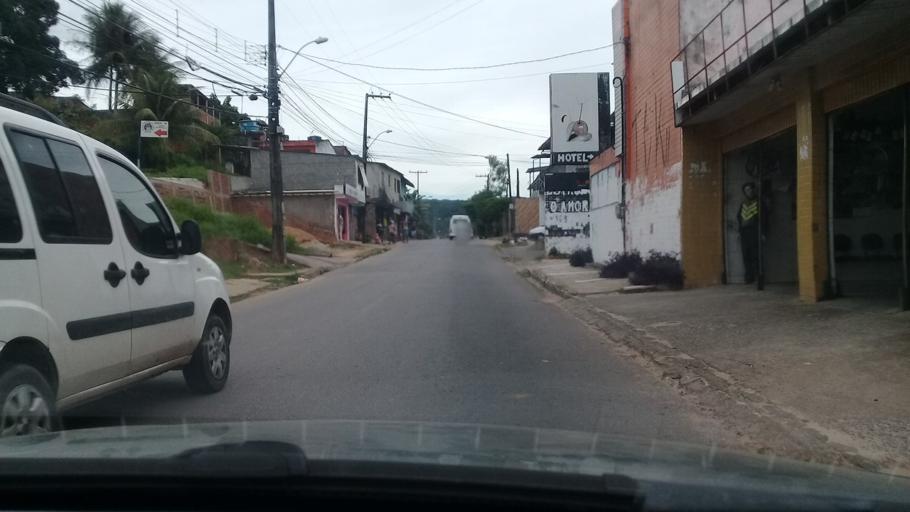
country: BR
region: Pernambuco
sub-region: Sao Lourenco Da Mata
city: Sao Lourenco da Mata
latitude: -8.0344
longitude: -34.9610
